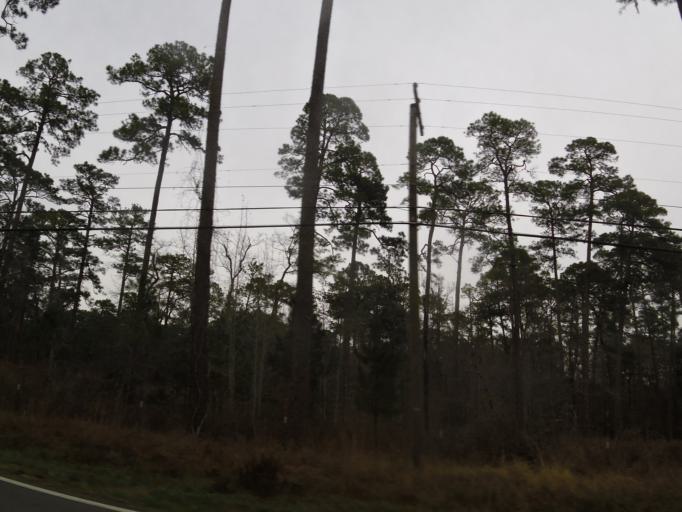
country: US
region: Georgia
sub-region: Thomas County
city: Thomasville
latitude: 30.8614
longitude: -84.0266
